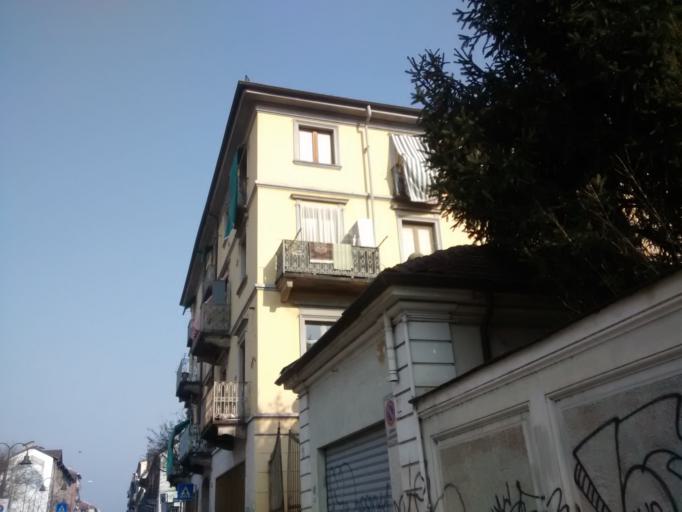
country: IT
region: Piedmont
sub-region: Provincia di Torino
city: Turin
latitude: 45.0918
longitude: 7.6756
